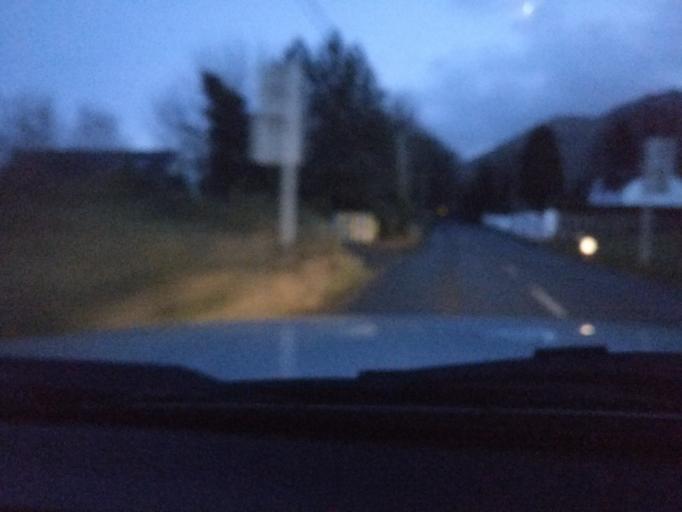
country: GB
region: Northern Ireland
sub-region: Down District
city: Warrenpoint
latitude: 54.0772
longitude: -6.2465
